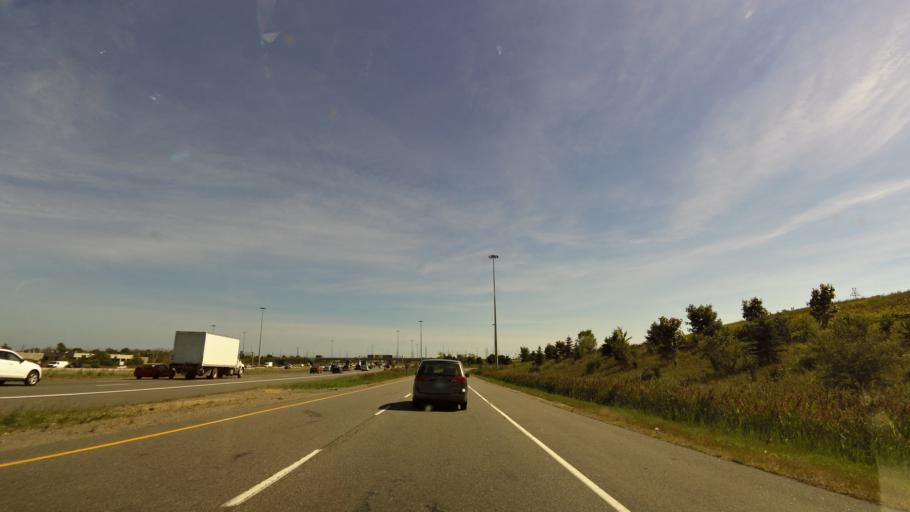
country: CA
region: Ontario
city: Mississauga
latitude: 43.6244
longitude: -79.6413
